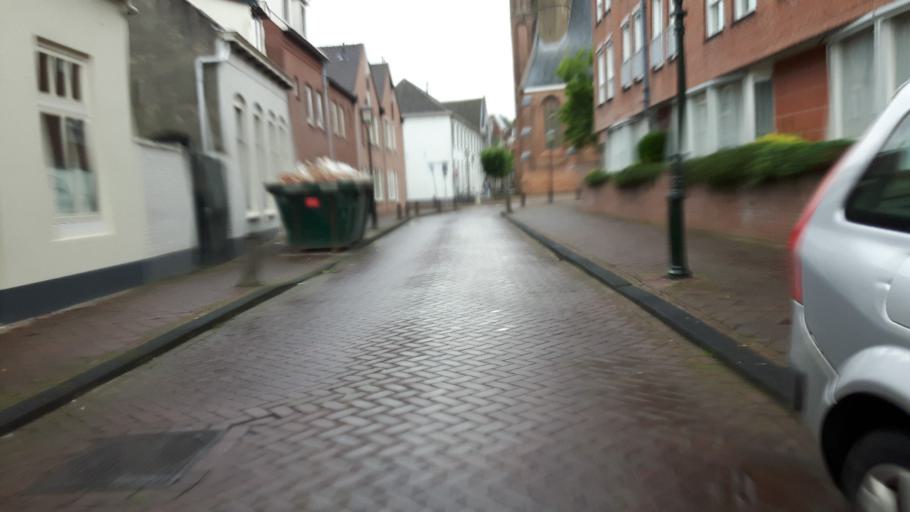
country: NL
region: Utrecht
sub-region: Gemeente Montfoort
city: Montfoort
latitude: 52.0444
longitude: 4.9484
